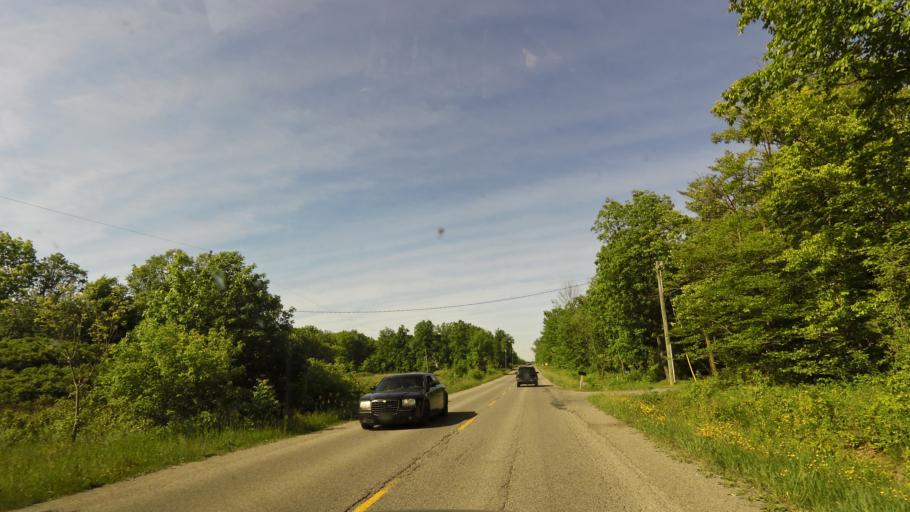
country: CA
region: Ontario
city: Ancaster
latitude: 43.0457
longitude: -80.0322
